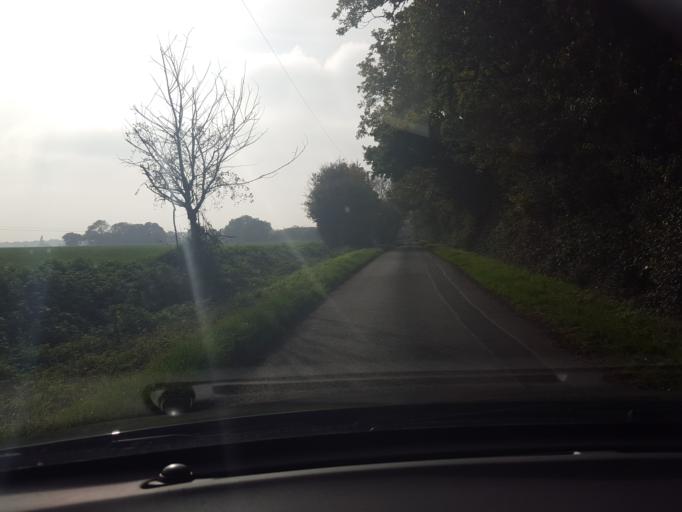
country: GB
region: England
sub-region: Essex
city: Mistley
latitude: 51.9232
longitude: 1.1490
